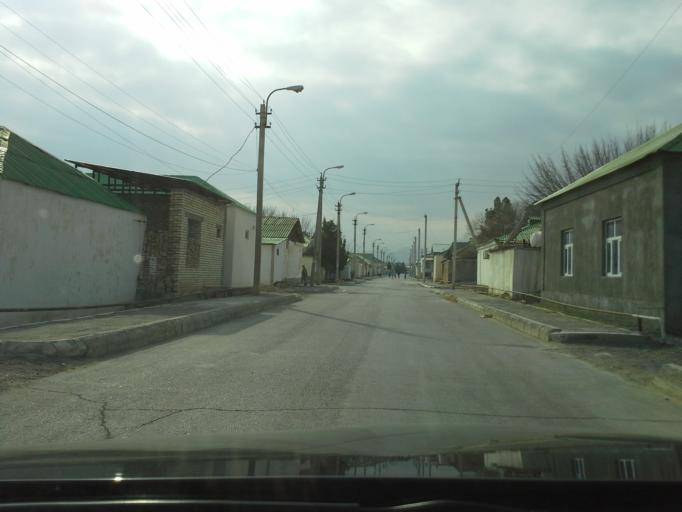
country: TM
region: Ahal
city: Abadan
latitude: 38.0417
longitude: 58.2776
